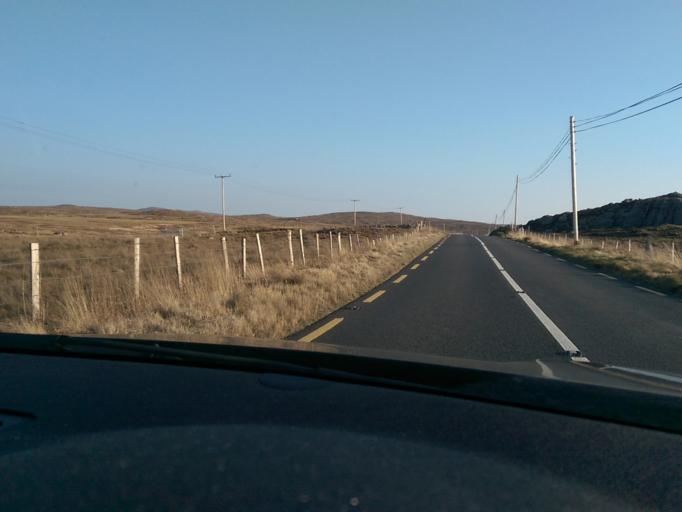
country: IE
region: Connaught
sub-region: County Galway
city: Oughterard
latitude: 53.3577
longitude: -9.5425
